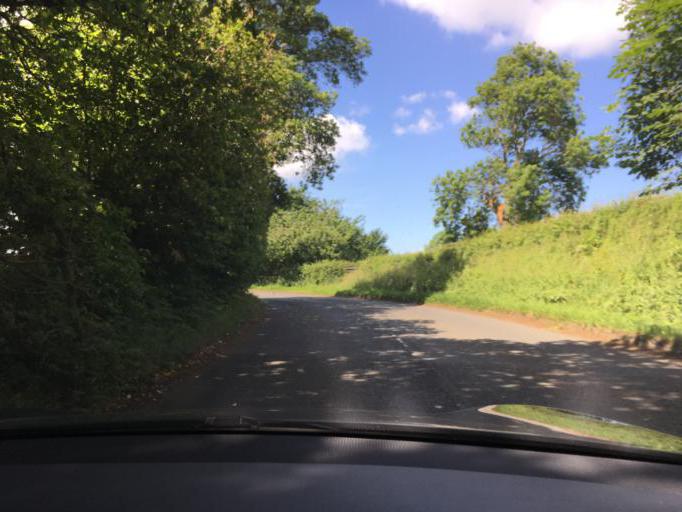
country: GB
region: England
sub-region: Manchester
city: Ringway
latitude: 53.3300
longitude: -2.2756
